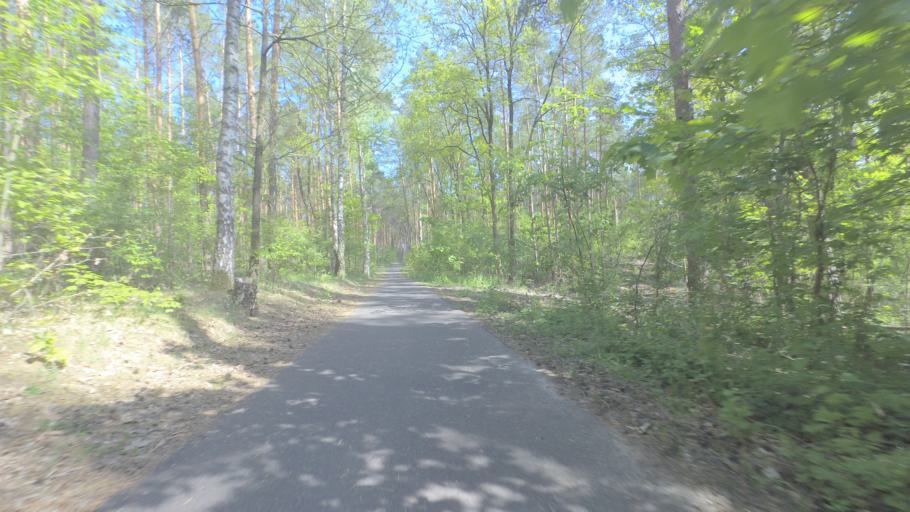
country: DE
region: Brandenburg
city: Grunheide
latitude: 52.4166
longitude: 13.8166
